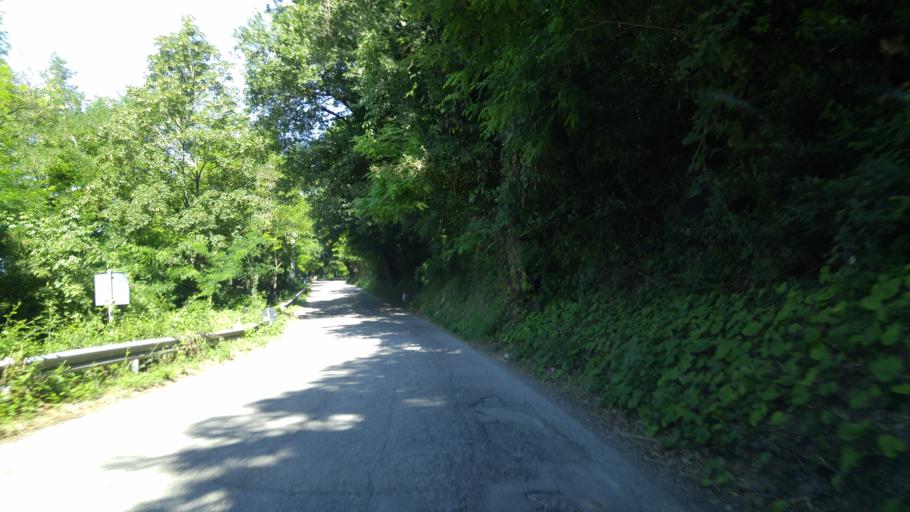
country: IT
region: The Marches
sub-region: Provincia di Pesaro e Urbino
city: Monteciccardo
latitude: 43.8246
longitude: 12.8054
